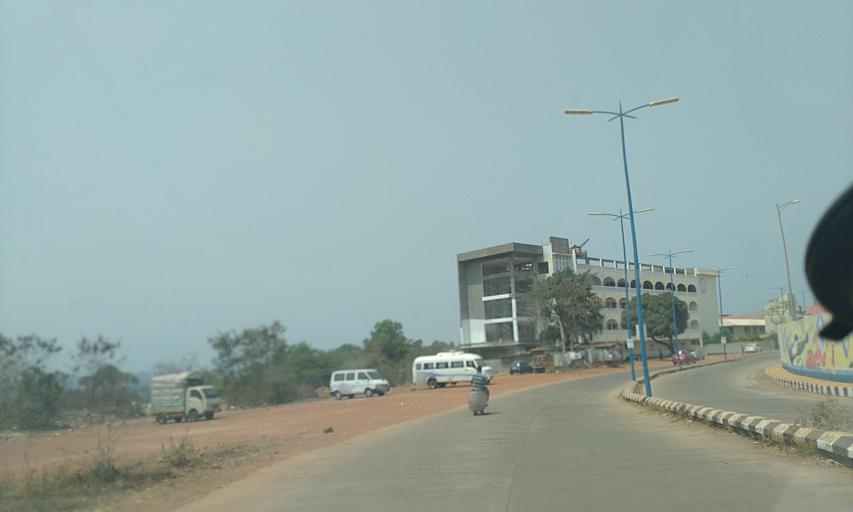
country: IN
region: Goa
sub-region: North Goa
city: Bambolim
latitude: 15.4667
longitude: 73.8602
